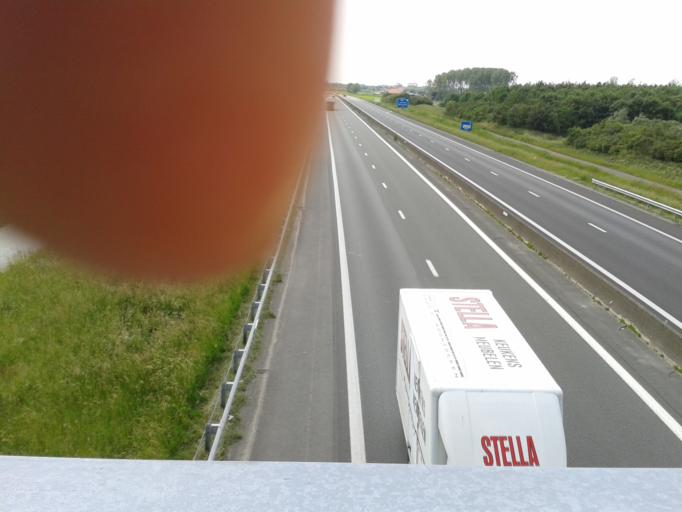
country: BE
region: Flanders
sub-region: Provincie West-Vlaanderen
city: Veurne
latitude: 51.0666
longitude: 2.6267
